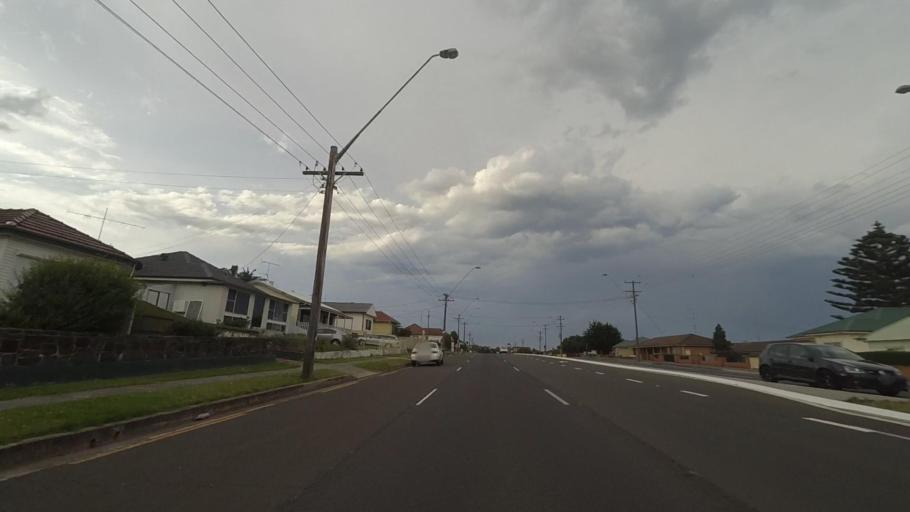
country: AU
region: New South Wales
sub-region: Shellharbour
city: Lake Illawarra
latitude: -34.5563
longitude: 150.8596
